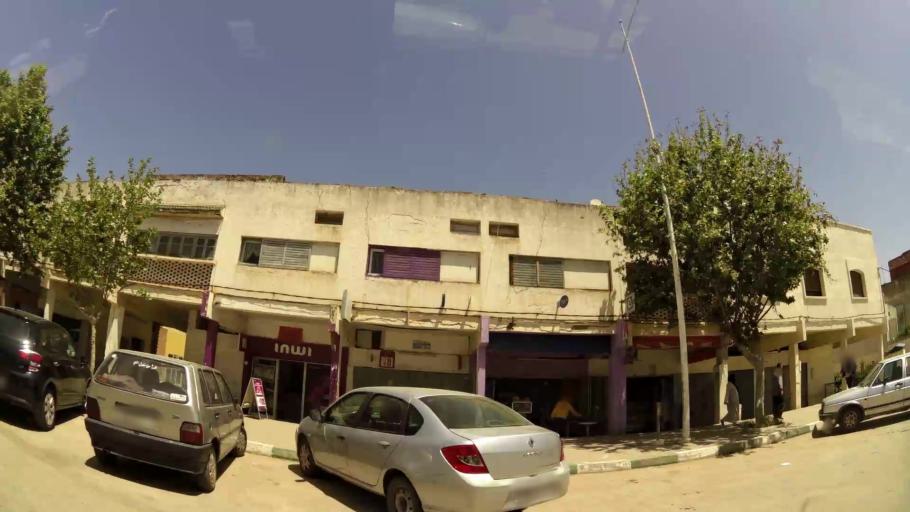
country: MA
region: Rabat-Sale-Zemmour-Zaer
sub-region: Khemisset
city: Khemisset
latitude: 33.8261
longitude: -6.0737
